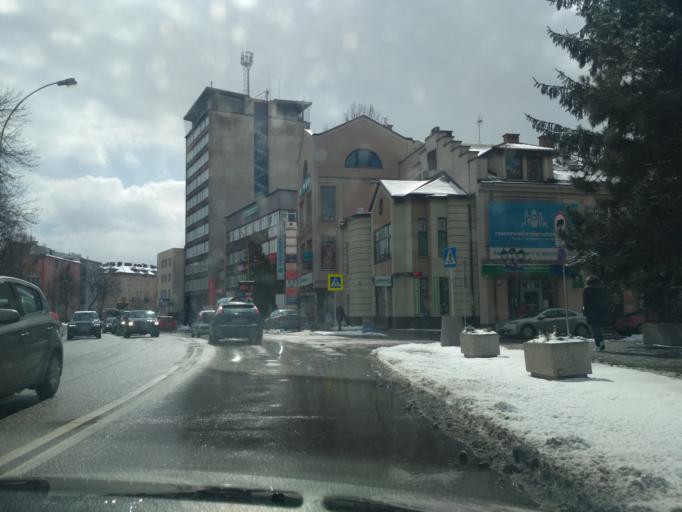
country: PL
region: Subcarpathian Voivodeship
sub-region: Rzeszow
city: Rzeszow
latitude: 50.0378
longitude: 22.0097
